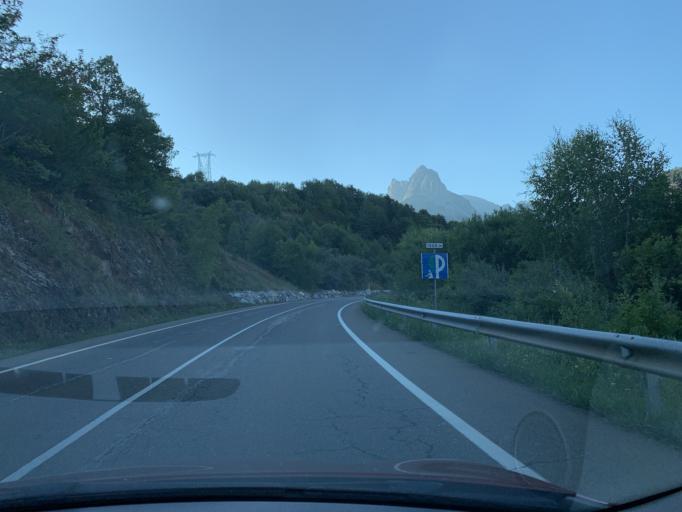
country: ES
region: Aragon
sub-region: Provincia de Huesca
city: Sallent de Gallego
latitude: 42.7539
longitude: -0.3193
